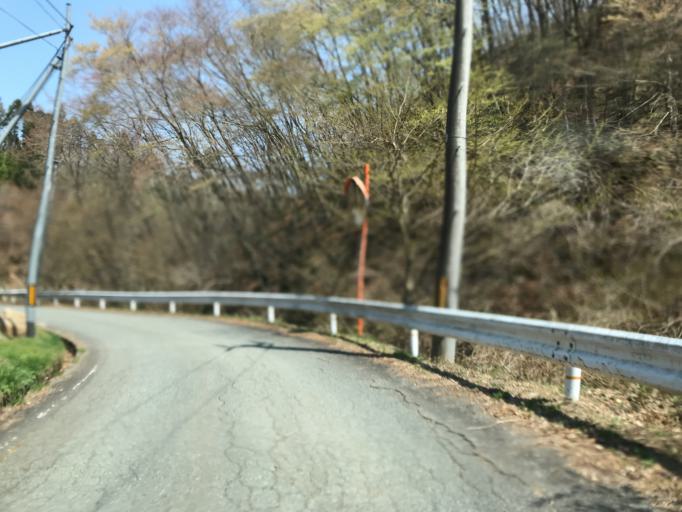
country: JP
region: Fukushima
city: Ishikawa
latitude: 36.9935
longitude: 140.5836
